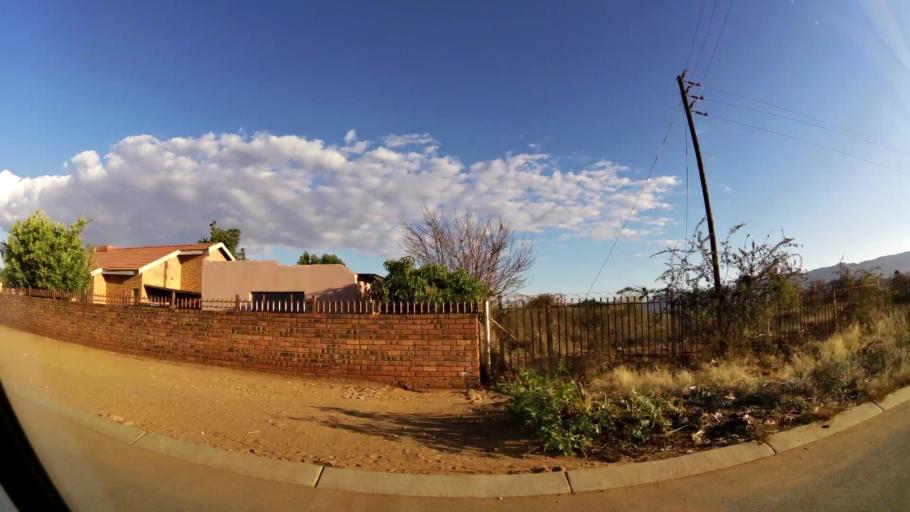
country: ZA
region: Limpopo
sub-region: Waterberg District Municipality
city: Mokopane
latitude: -24.1464
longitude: 28.9959
